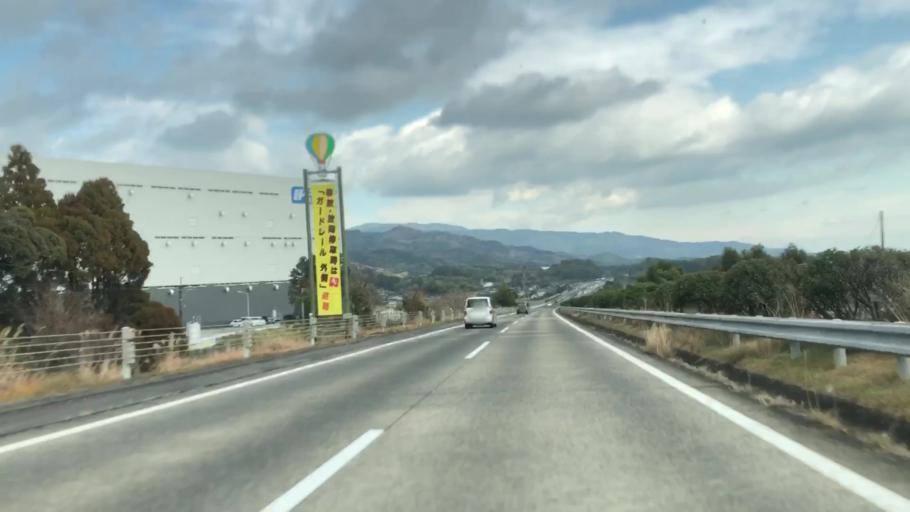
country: JP
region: Saga Prefecture
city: Kanzakimachi-kanzaki
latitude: 33.3435
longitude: 130.3604
